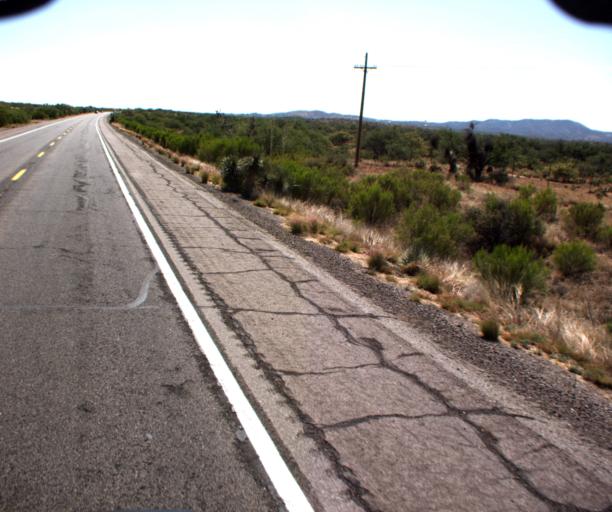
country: US
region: Arizona
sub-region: Pinal County
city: Oracle
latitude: 32.6098
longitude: -110.8485
